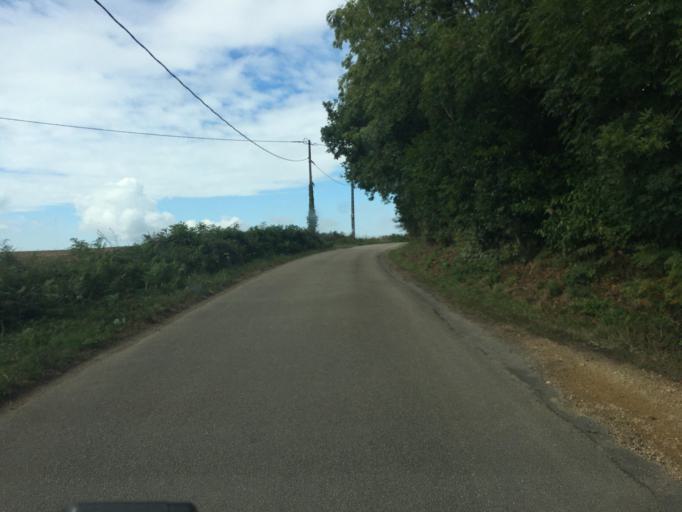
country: FR
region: Brittany
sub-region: Departement du Finistere
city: Beuzec-Cap-Sizun
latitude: 48.0752
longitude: -4.4956
